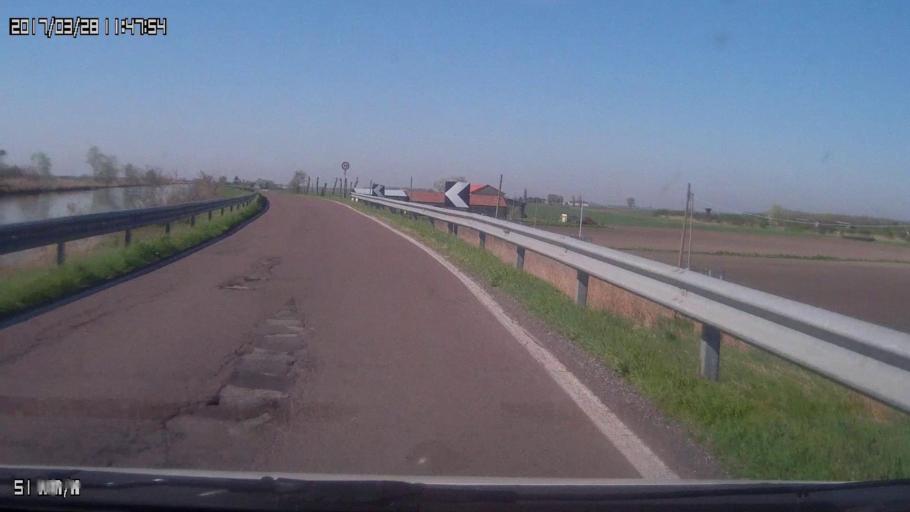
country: IT
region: Veneto
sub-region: Provincia di Venezia
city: Sant'Anna
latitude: 45.1643
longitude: 12.2285
